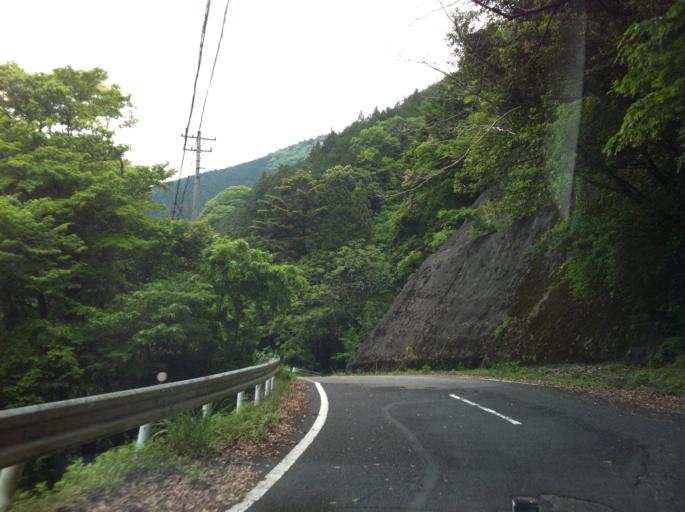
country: JP
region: Shizuoka
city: Shizuoka-shi
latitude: 35.1652
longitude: 138.3254
